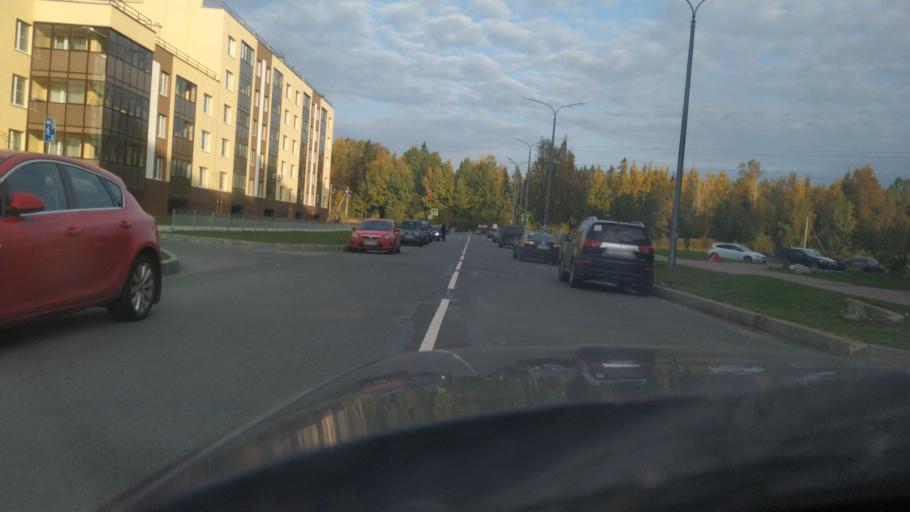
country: RU
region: Leningrad
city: Sosnovyy Bor
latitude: 59.9168
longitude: 29.0834
